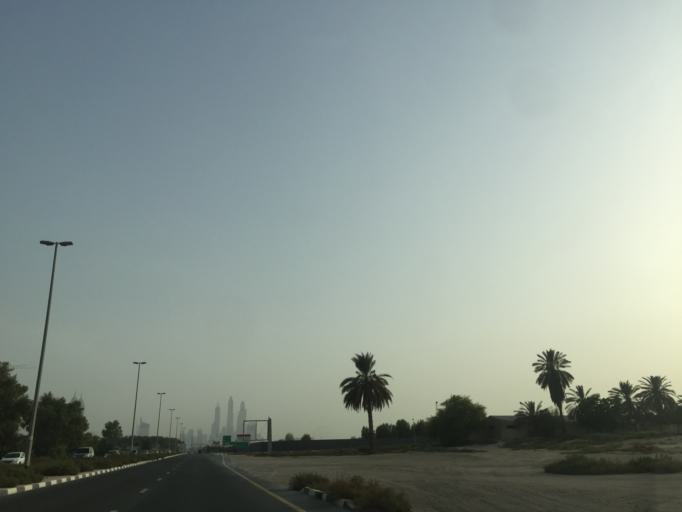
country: AE
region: Dubai
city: Dubai
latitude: 25.1225
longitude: 55.1839
